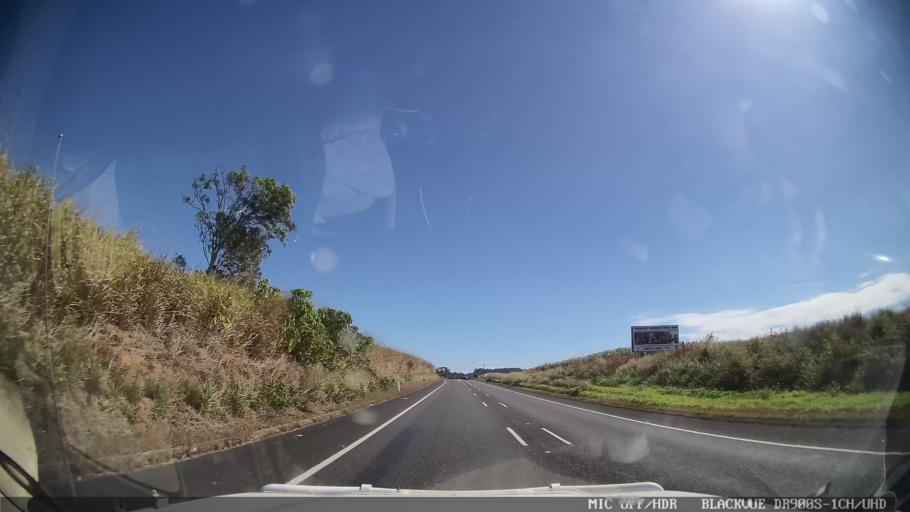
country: AU
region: Queensland
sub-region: Mackay
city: Walkerston
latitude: -21.0903
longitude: 149.0475
